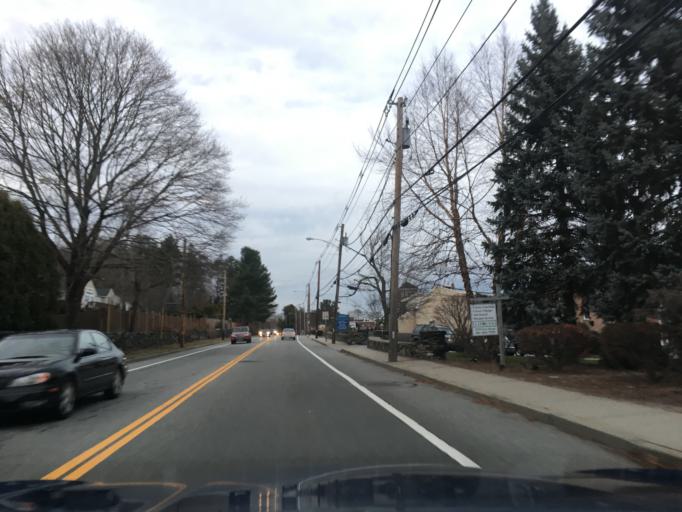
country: US
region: Rhode Island
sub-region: Kent County
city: East Greenwich
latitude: 41.6796
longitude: -71.4494
